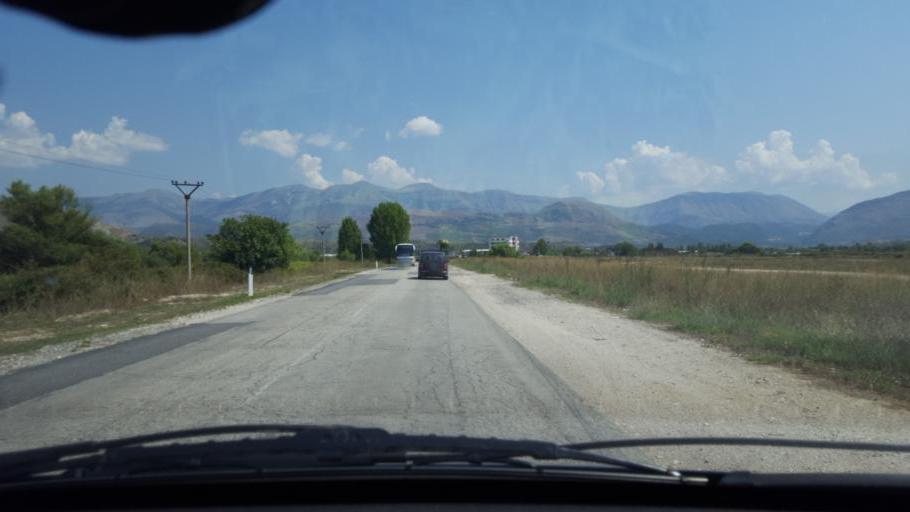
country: AL
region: Vlore
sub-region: Rrethi i Delvines
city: Finiq
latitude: 39.8870
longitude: 20.0591
